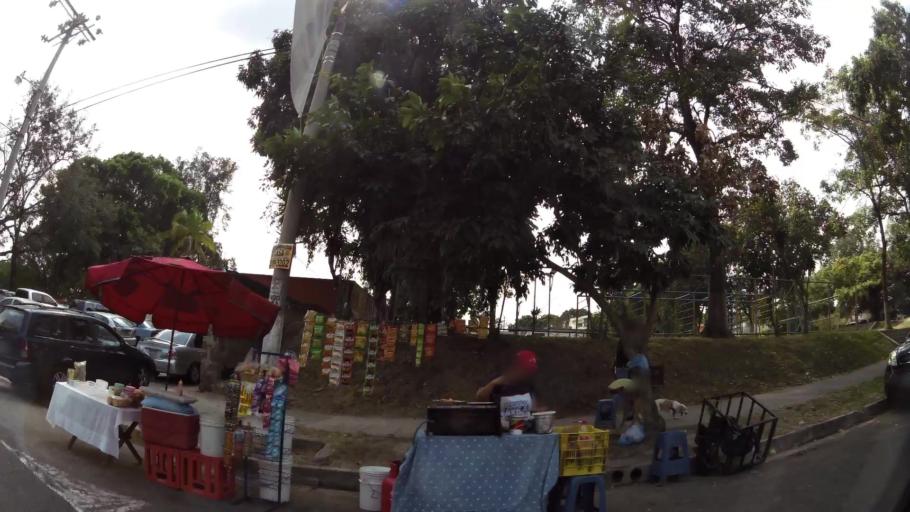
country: SV
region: San Salvador
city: Mejicanos
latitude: 13.7130
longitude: -89.2138
